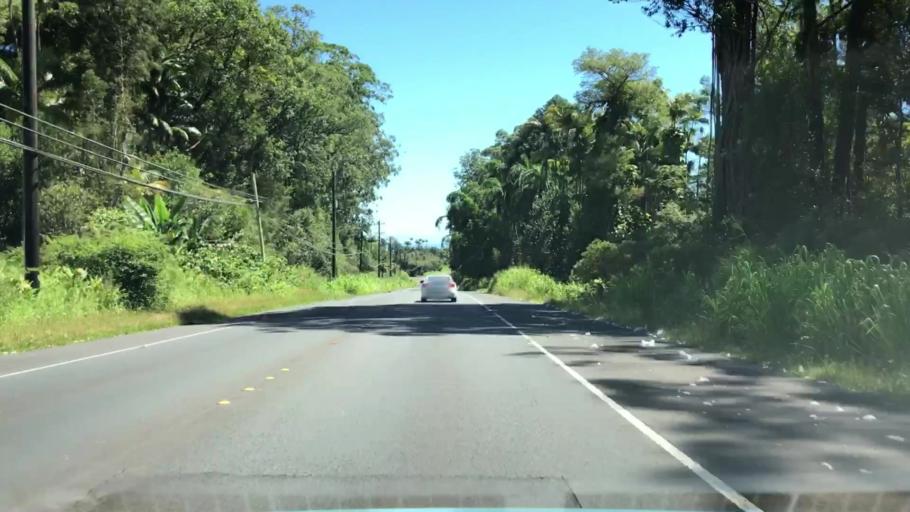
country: US
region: Hawaii
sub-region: Hawaii County
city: Mountain View
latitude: 19.5443
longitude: -155.1158
